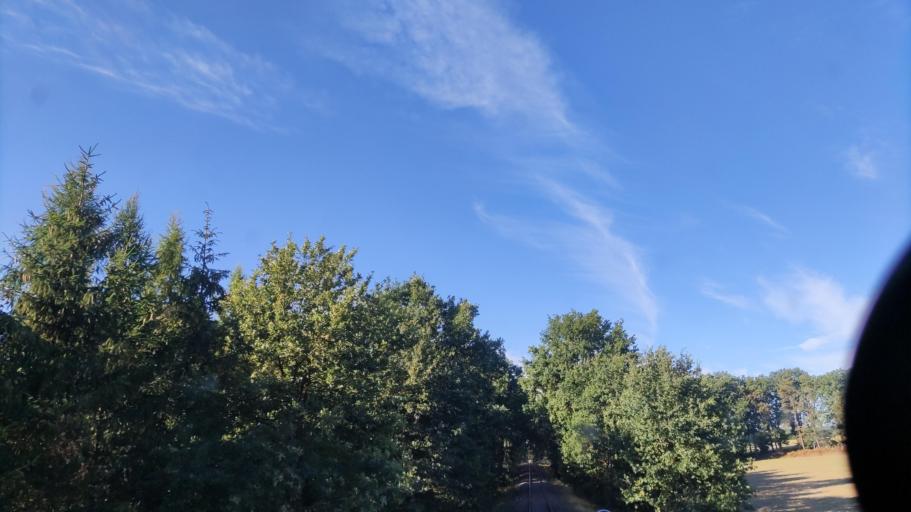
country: DE
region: Lower Saxony
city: Embsen
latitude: 53.1653
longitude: 10.3575
